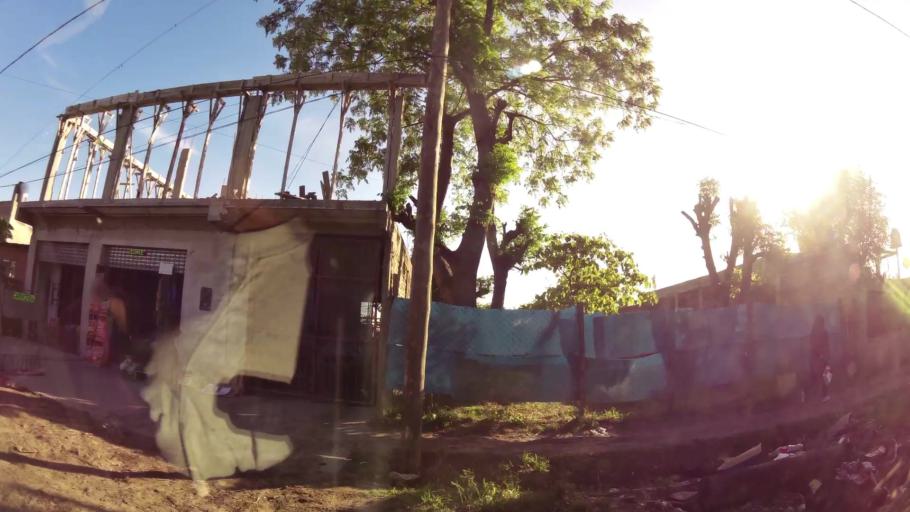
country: AR
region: Buenos Aires
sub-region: Partido de Quilmes
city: Quilmes
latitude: -34.8208
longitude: -58.2144
